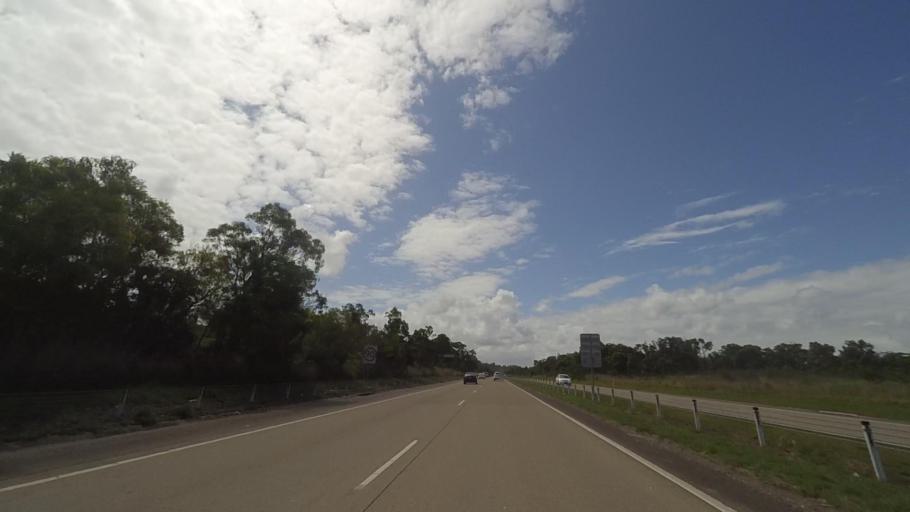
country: AU
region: New South Wales
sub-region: Lake Macquarie Shire
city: Windale
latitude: -32.9892
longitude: 151.6871
